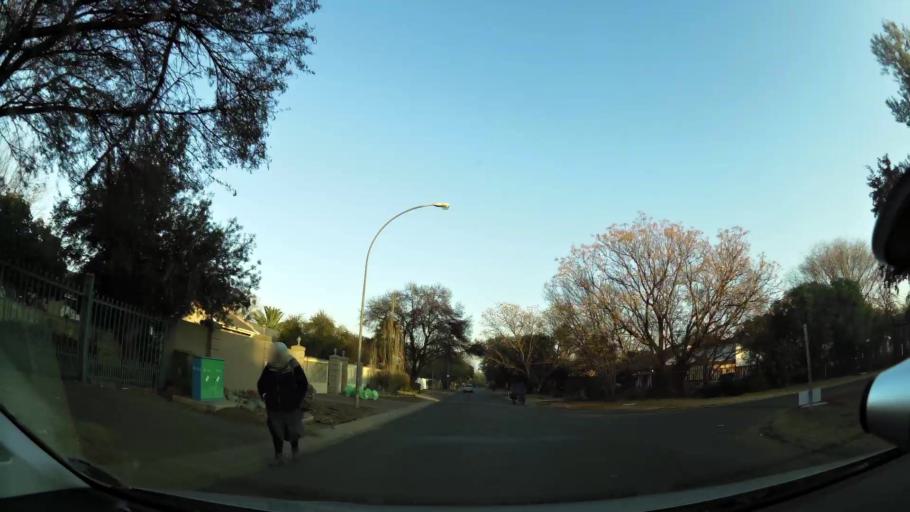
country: ZA
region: Orange Free State
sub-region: Mangaung Metropolitan Municipality
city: Bloemfontein
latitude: -29.1080
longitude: 26.1579
